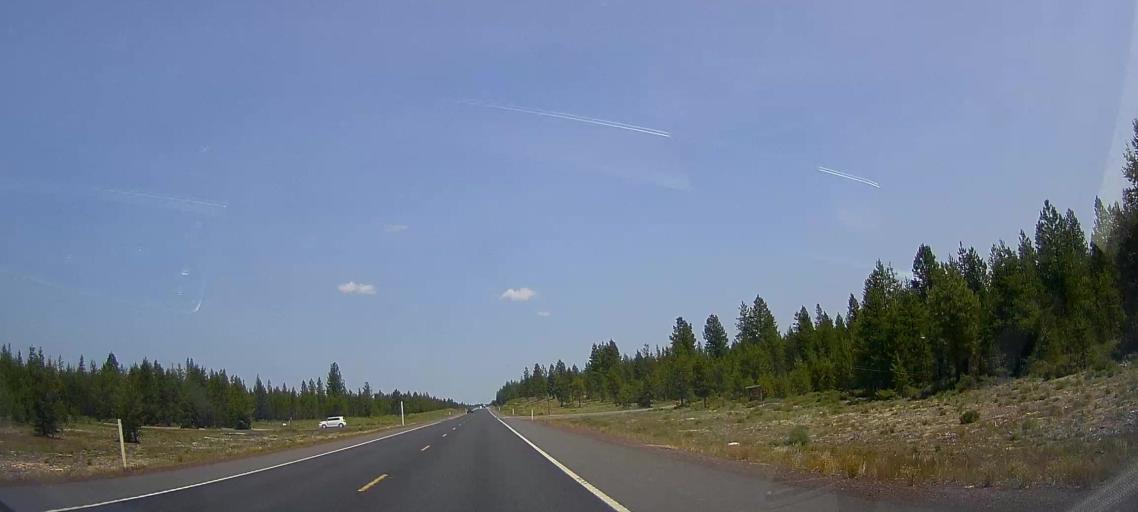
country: US
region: Oregon
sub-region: Deschutes County
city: La Pine
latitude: 43.5067
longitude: -121.6628
